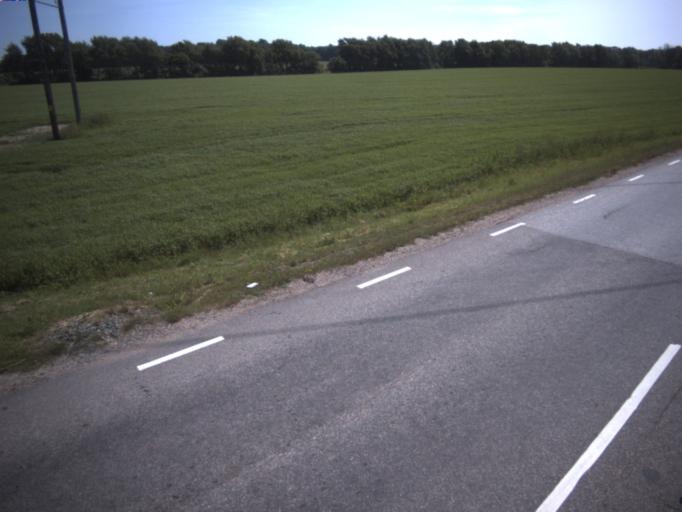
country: SE
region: Skane
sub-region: Helsingborg
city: Helsingborg
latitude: 56.0944
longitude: 12.6799
